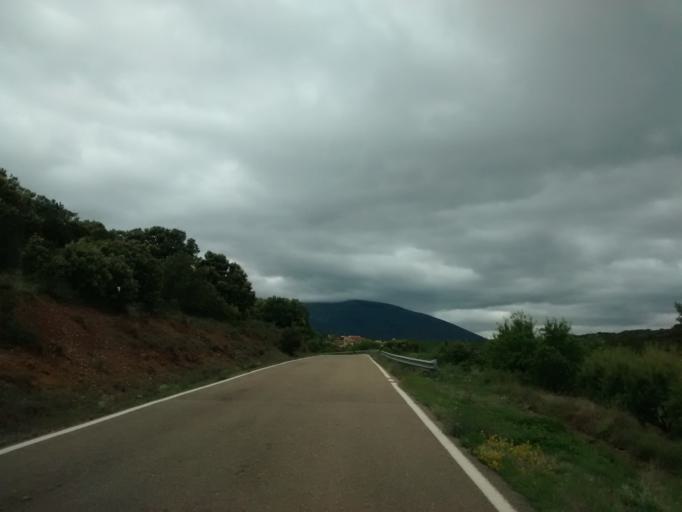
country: ES
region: Aragon
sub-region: Provincia de Zaragoza
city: Lituenigo
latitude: 41.8380
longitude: -1.7538
